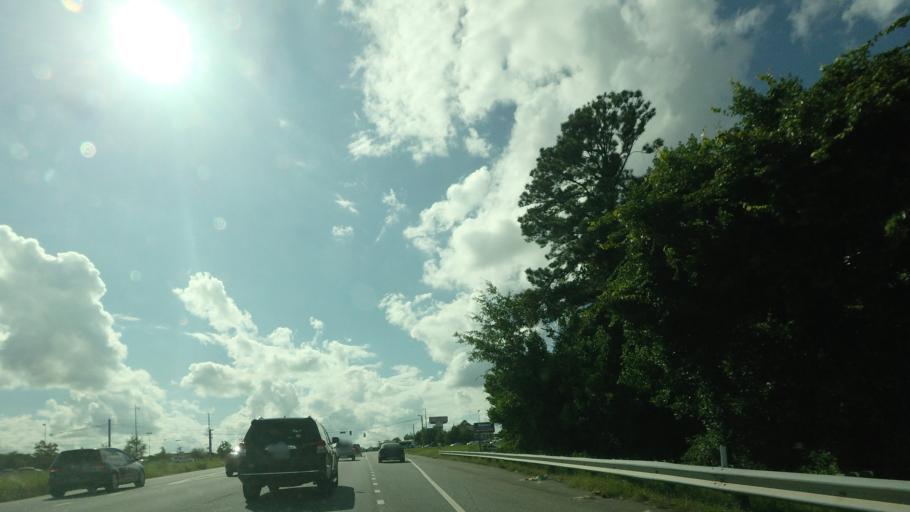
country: US
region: Georgia
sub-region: Bibb County
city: Macon
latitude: 32.8165
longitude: -83.7070
